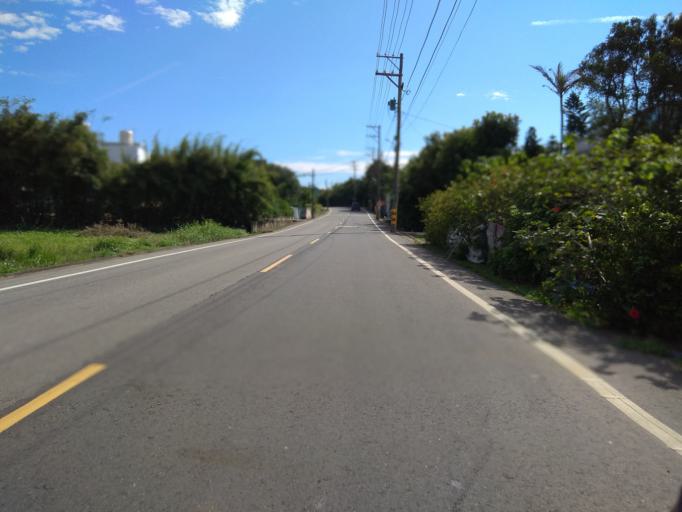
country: TW
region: Taiwan
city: Taoyuan City
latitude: 25.0413
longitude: 121.1246
